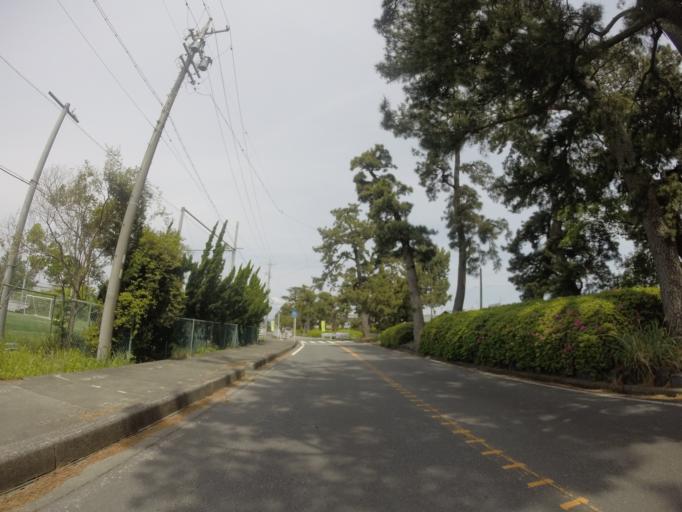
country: JP
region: Shizuoka
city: Yaizu
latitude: 34.8392
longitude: 138.3326
